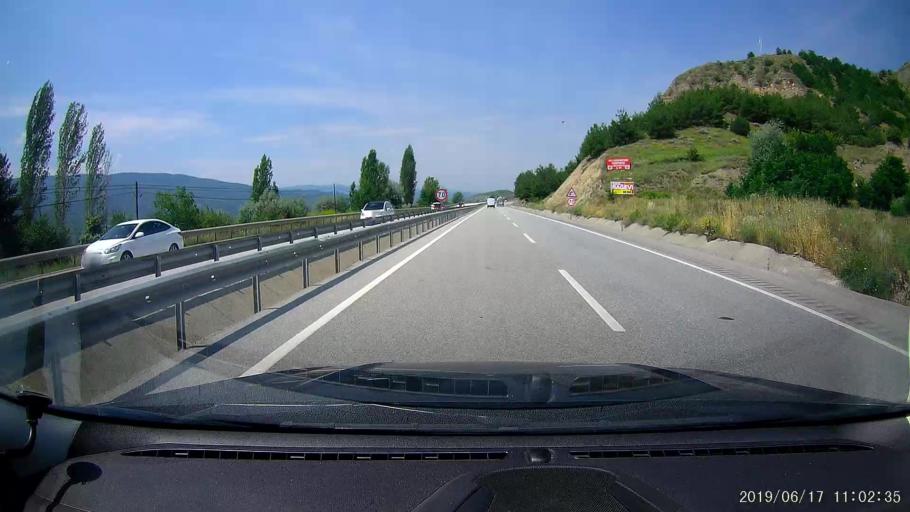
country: TR
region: Kastamonu
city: Tosya
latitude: 41.0165
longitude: 34.1333
